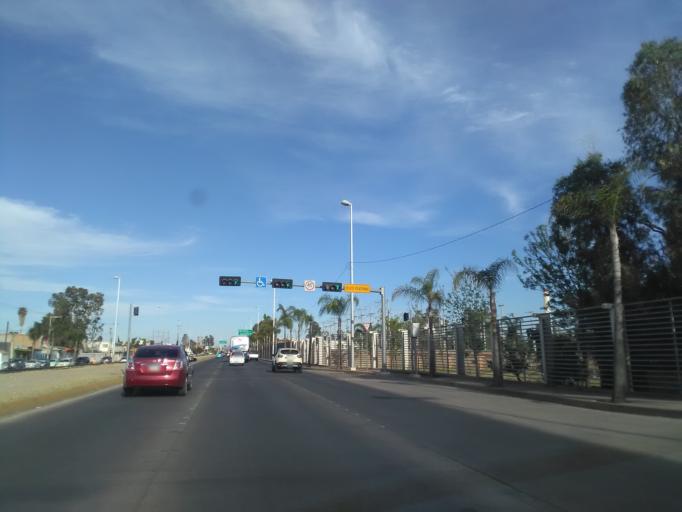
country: MX
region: Durango
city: Victoria de Durango
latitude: 24.0361
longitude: -104.6440
